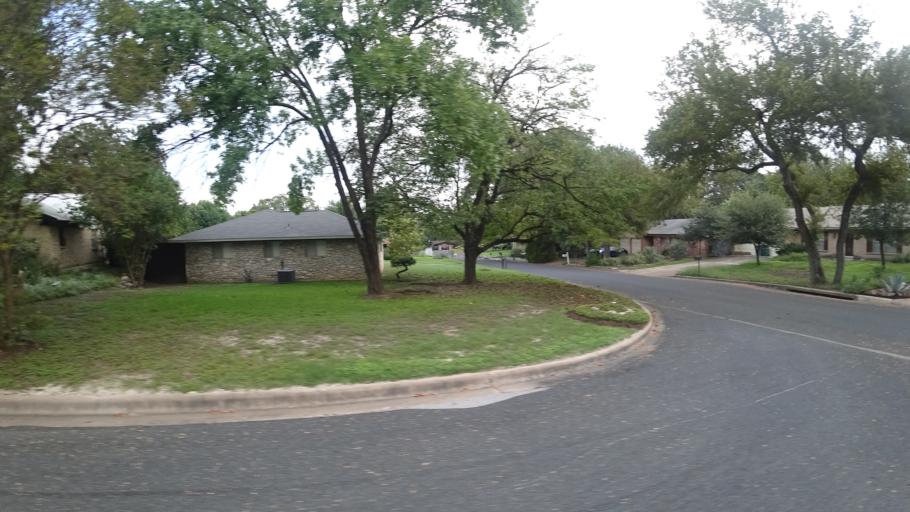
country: US
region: Texas
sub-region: Travis County
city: Austin
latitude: 30.3479
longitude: -97.6907
